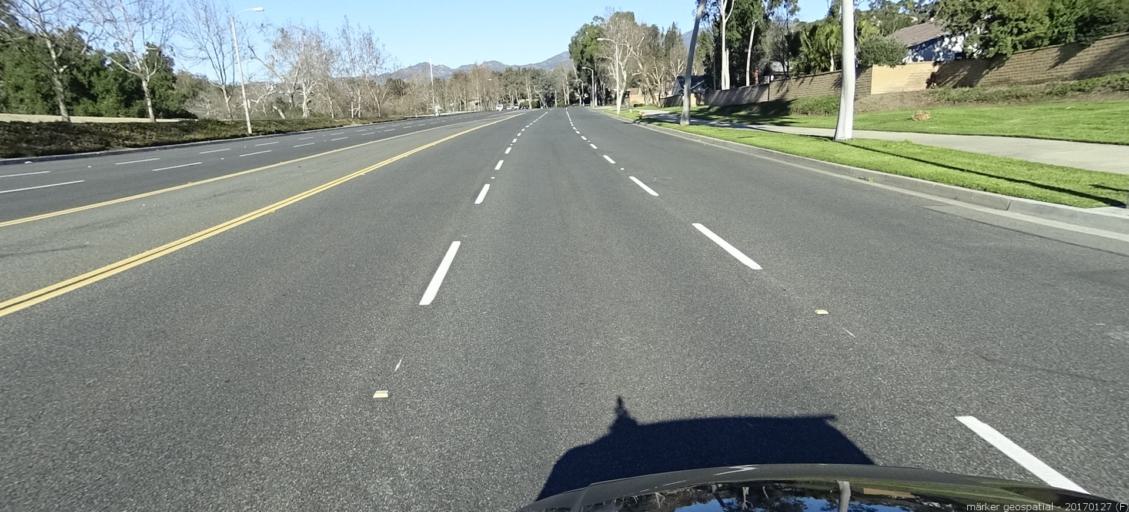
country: US
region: California
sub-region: Orange County
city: Lake Forest
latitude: 33.6464
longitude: -117.6638
